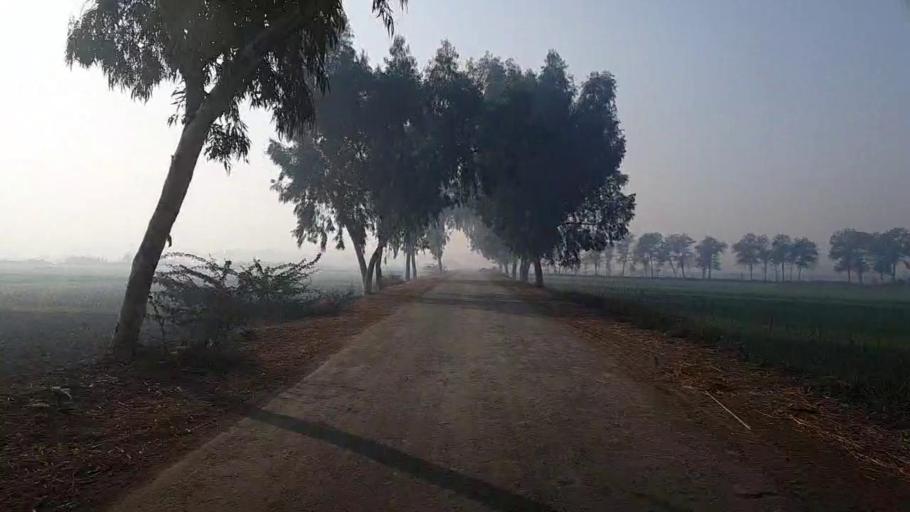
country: PK
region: Sindh
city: Mehar
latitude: 27.1408
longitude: 67.8231
